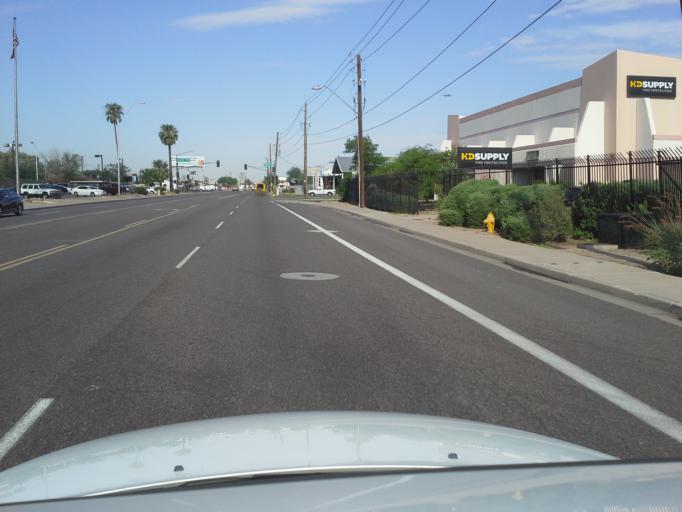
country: US
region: Arizona
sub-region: Maricopa County
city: Phoenix
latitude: 33.4369
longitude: -112.0504
